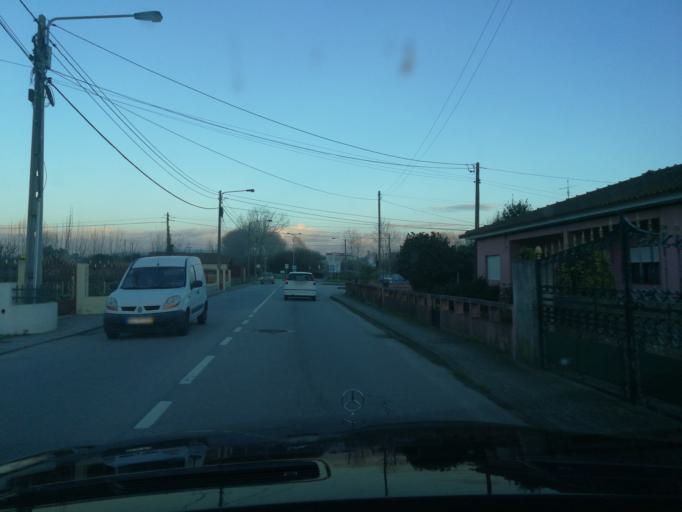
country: PT
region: Aveiro
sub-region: Estarreja
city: Estarreja
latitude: 40.7557
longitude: -8.5822
